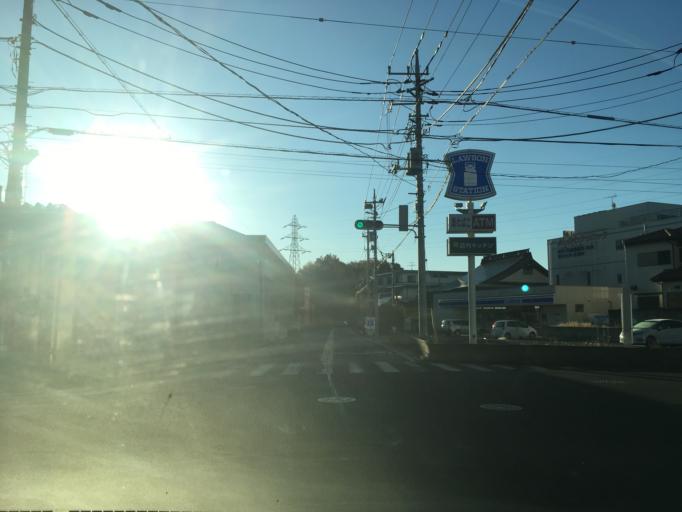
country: JP
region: Saitama
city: Tokorozawa
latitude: 35.8024
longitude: 139.4200
